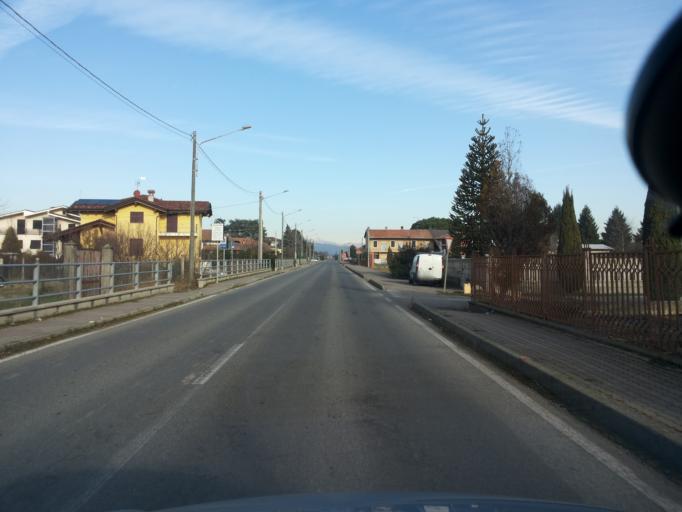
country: IT
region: Piedmont
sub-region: Provincia di Vercelli
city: Ghislarengo
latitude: 45.5317
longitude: 8.3858
